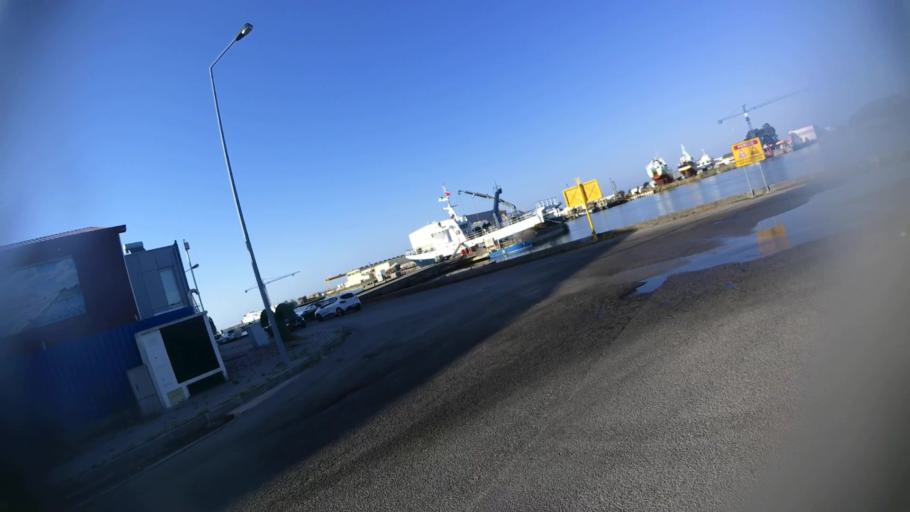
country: PT
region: Aveiro
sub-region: Ilhavo
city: Gafanha da Nazare
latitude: 40.6329
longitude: -8.6884
